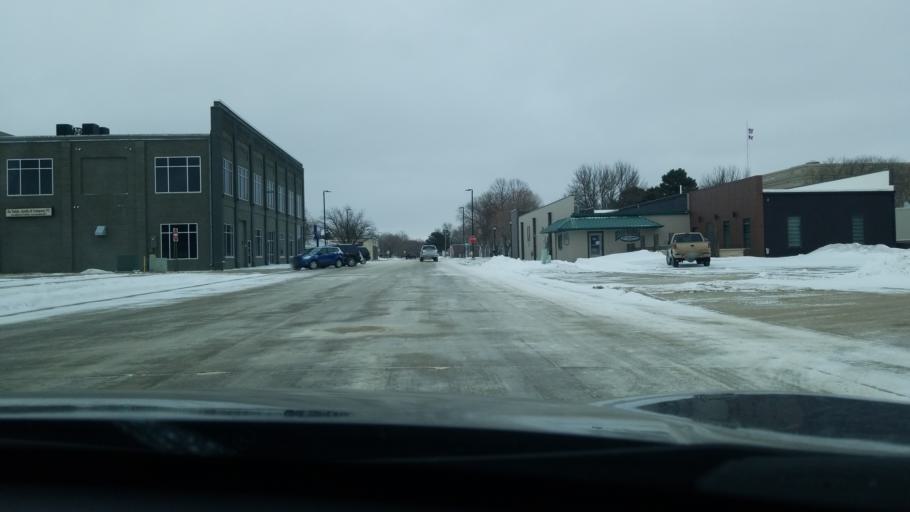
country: US
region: Iowa
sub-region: Lyon County
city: Rock Rapids
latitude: 43.4307
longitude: -96.1693
